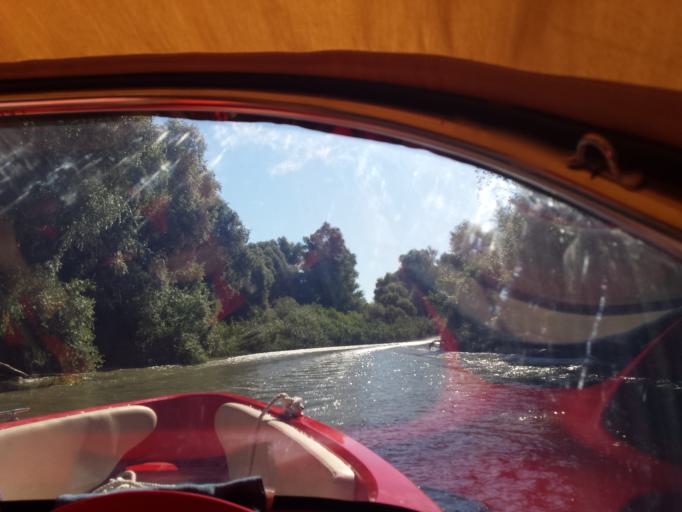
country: RO
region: Tulcea
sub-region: Comuna Pardina
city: Pardina
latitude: 45.2477
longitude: 29.0180
